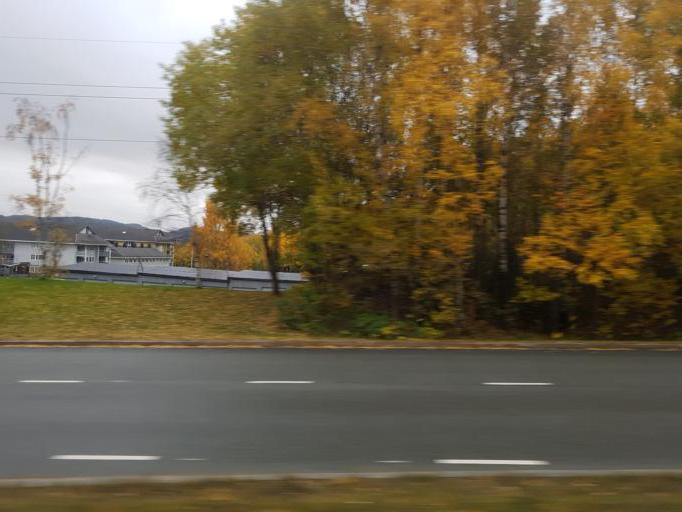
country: NO
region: Sor-Trondelag
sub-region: Trondheim
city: Trondheim
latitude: 63.3719
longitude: 10.3465
